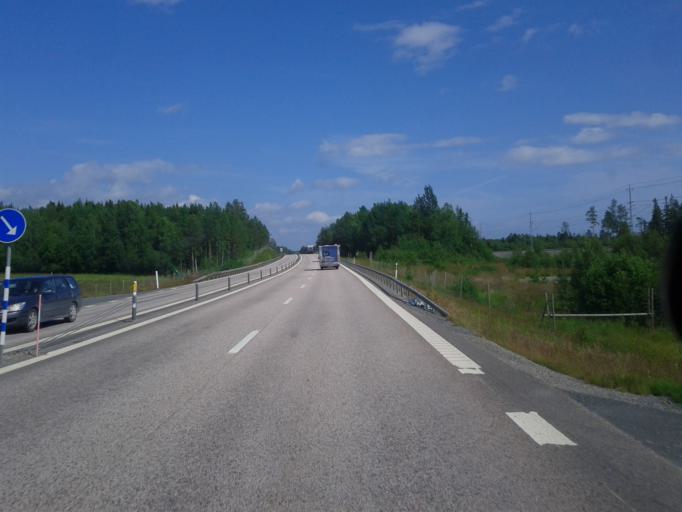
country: SE
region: Vaesterbotten
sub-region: Nordmalings Kommun
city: Nordmaling
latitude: 63.5047
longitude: 19.3455
